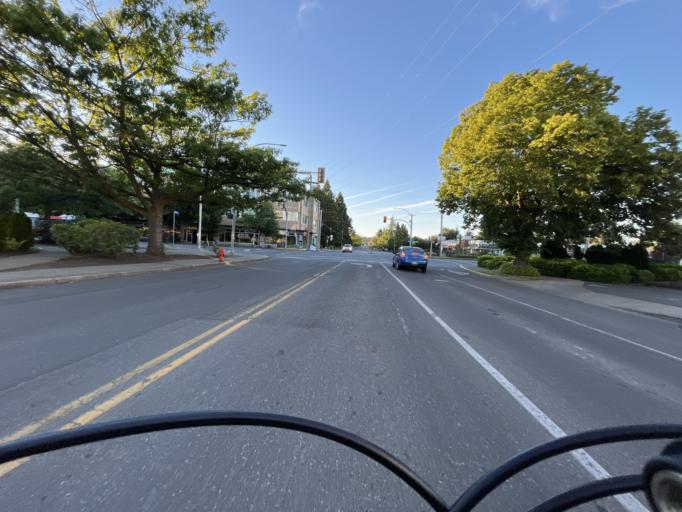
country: CA
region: British Columbia
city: Oak Bay
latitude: 48.4318
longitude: -123.3224
